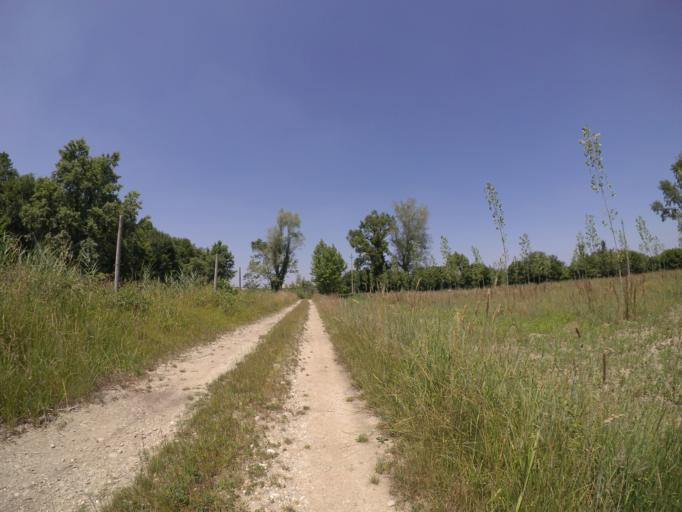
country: IT
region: Friuli Venezia Giulia
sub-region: Provincia di Udine
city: Rivignano
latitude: 45.9085
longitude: 13.0270
